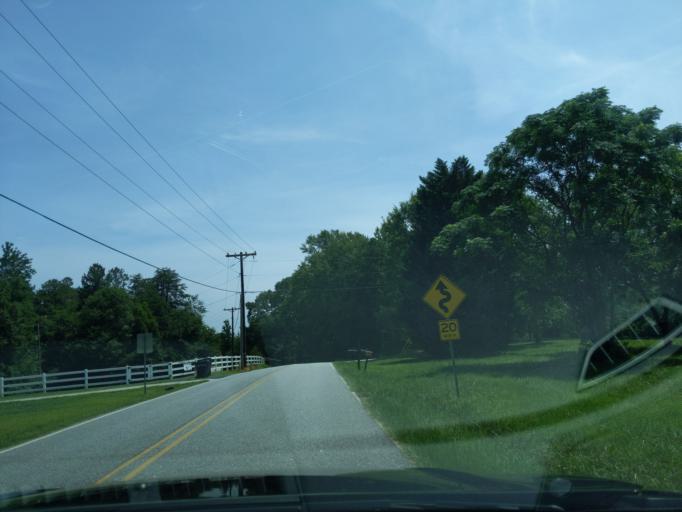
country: US
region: South Carolina
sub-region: Greenville County
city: Five Forks
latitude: 34.8323
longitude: -82.2172
